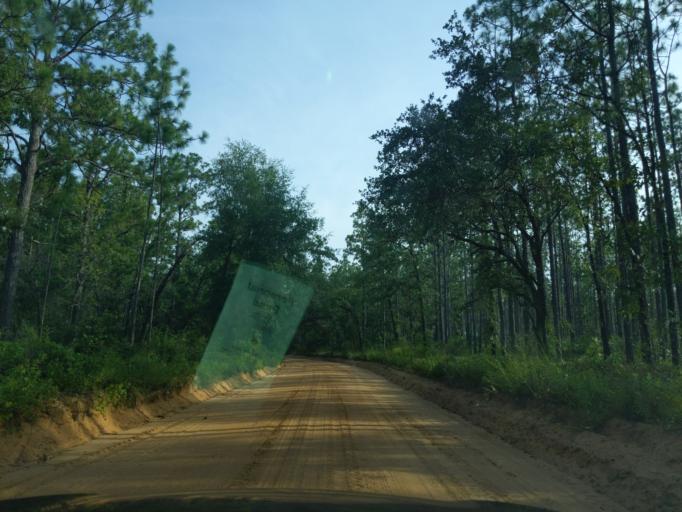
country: US
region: Florida
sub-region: Gadsden County
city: Midway
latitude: 30.3947
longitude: -84.4094
